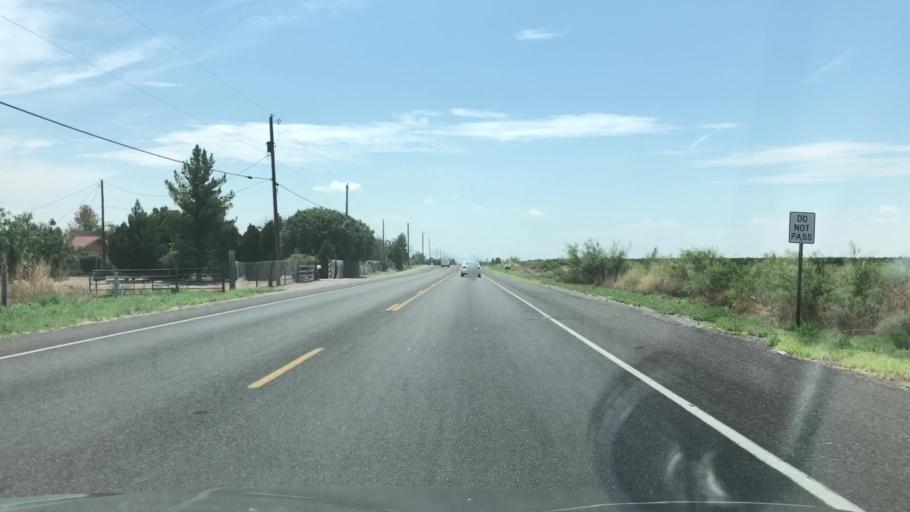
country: US
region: New Mexico
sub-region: Dona Ana County
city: Mesquite
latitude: 32.1892
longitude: -106.7122
